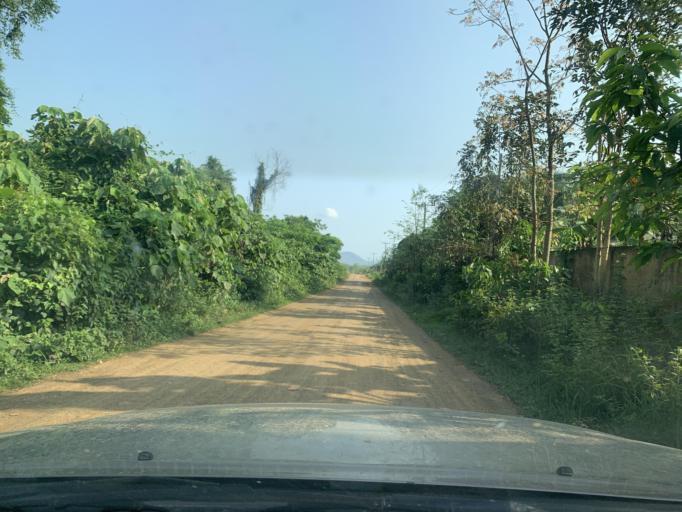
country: TH
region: Uttaradit
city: Ban Khok
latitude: 18.2769
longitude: 101.3060
